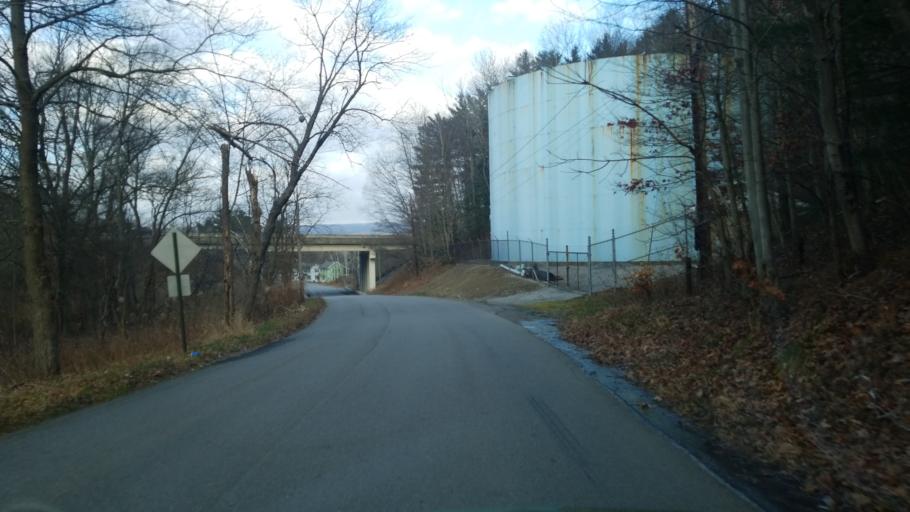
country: US
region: Pennsylvania
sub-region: Clearfield County
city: Clearfield
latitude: 41.0167
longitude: -78.4266
